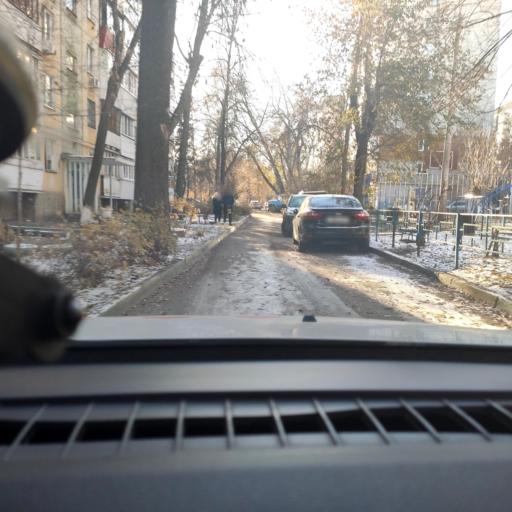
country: RU
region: Samara
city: Samara
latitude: 53.1972
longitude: 50.2233
